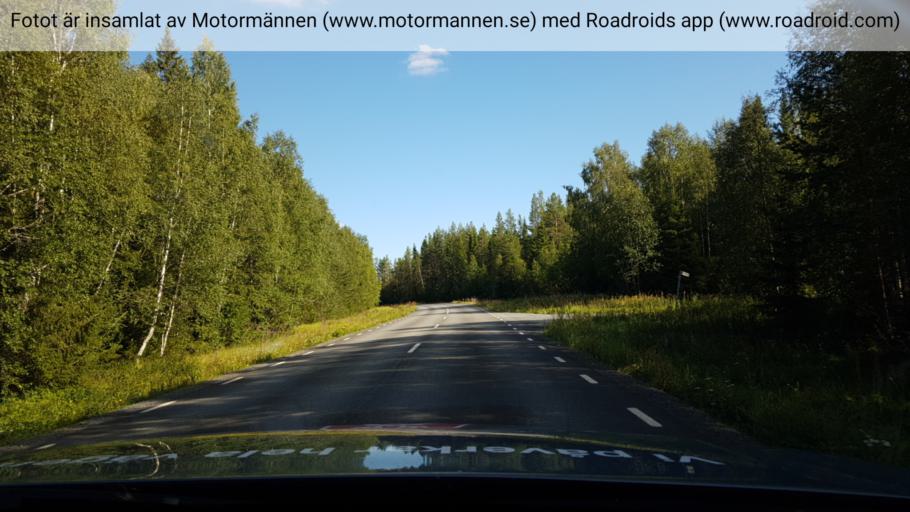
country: SE
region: Jaemtland
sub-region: OEstersunds Kommun
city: Lit
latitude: 63.3825
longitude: 14.7999
